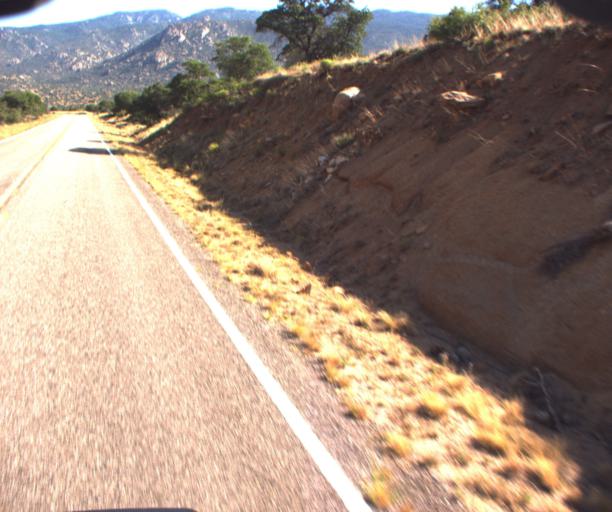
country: US
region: Arizona
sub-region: Graham County
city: Swift Trail Junction
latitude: 32.5875
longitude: -109.8543
